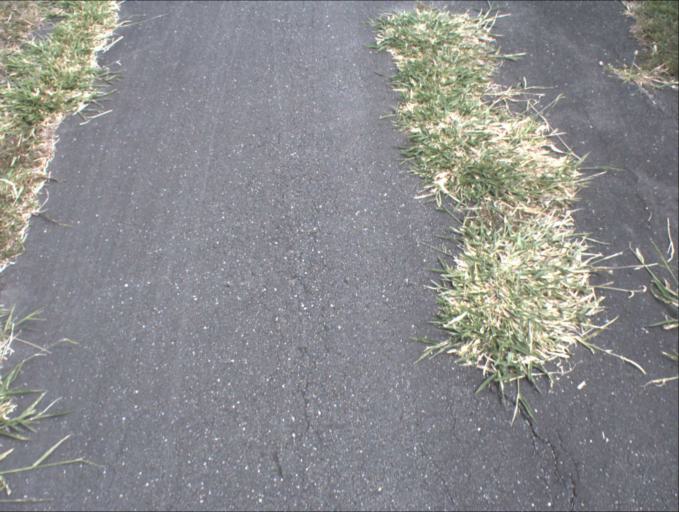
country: AU
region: Queensland
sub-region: Logan
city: Beenleigh
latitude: -27.6807
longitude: 153.1872
